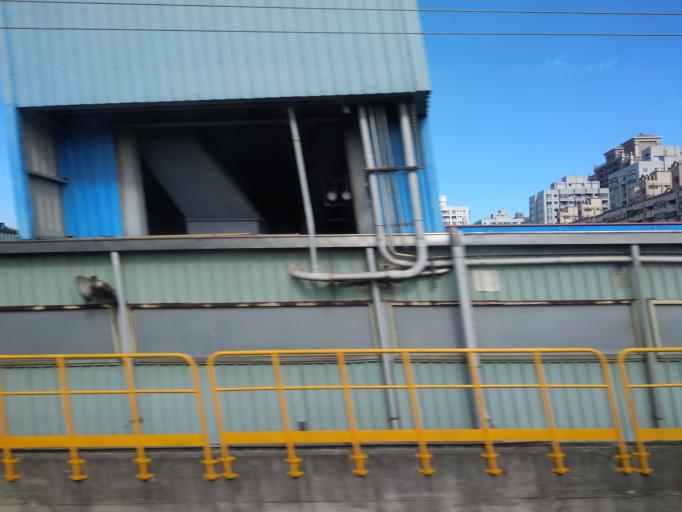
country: TW
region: Taiwan
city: Taoyuan City
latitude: 24.9837
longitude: 121.2870
